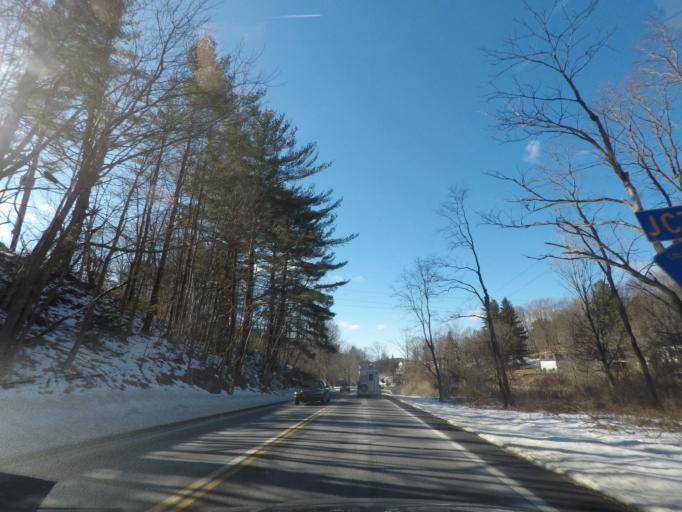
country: US
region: Massachusetts
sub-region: Berkshire County
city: Richmond
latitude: 42.4112
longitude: -73.4440
